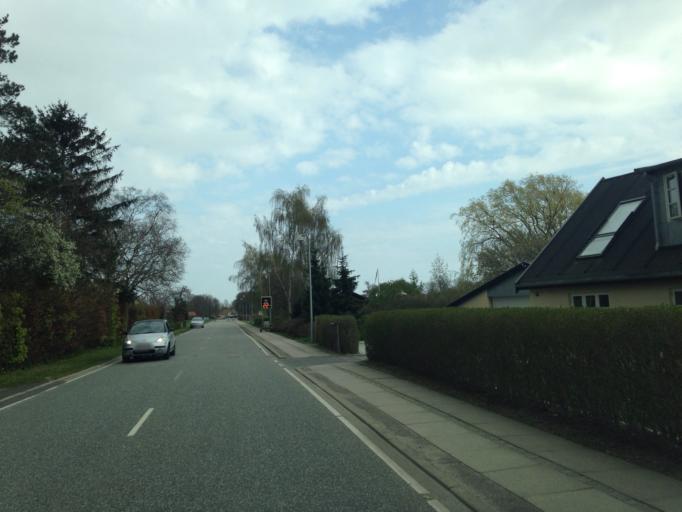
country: DK
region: Capital Region
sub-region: Hoje-Taastrup Kommune
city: Taastrup
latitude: 55.6281
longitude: 12.2914
